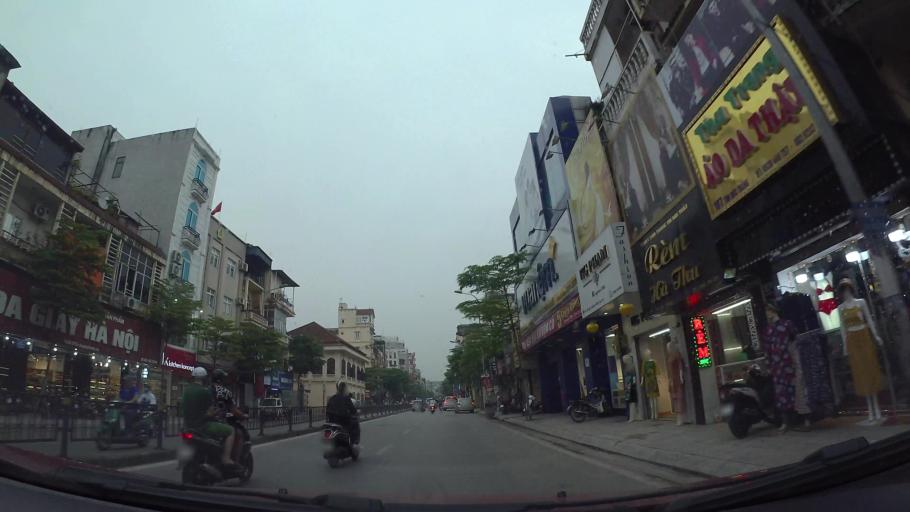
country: VN
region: Ha Noi
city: Dong Da
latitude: 21.0241
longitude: 105.8325
